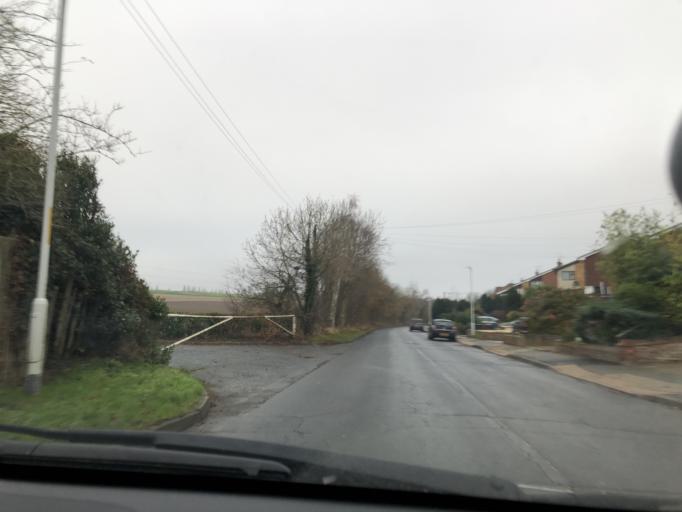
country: GB
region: England
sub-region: Kent
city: Meopham
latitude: 51.4056
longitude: 0.3440
